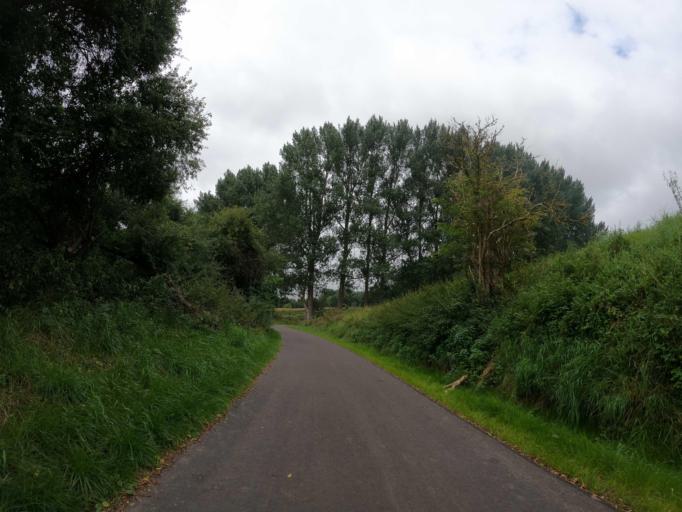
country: DE
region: Mecklenburg-Vorpommern
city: Rambin
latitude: 54.2972
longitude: 13.2143
